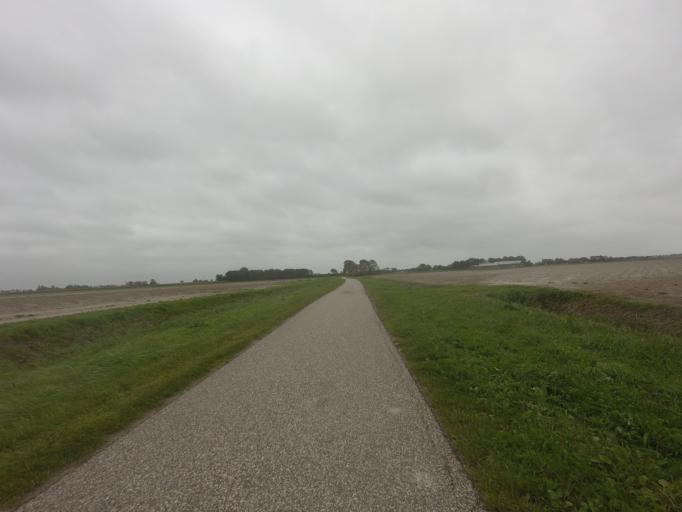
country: NL
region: Friesland
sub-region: Gemeente Ferwerderadiel
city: Ferwert
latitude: 53.3419
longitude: 5.8574
